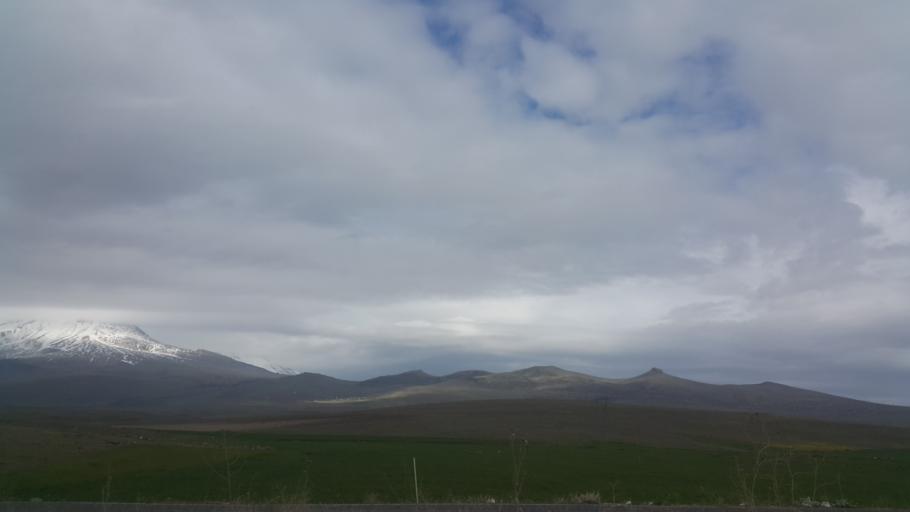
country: TR
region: Aksaray
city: Taspinar
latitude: 38.0776
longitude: 34.0328
